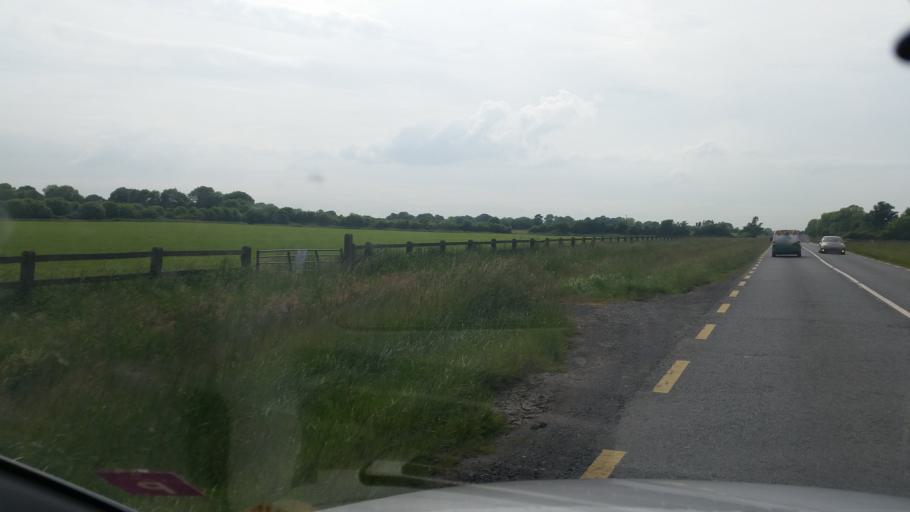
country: IE
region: Leinster
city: Ballymun
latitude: 53.4384
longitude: -6.2675
